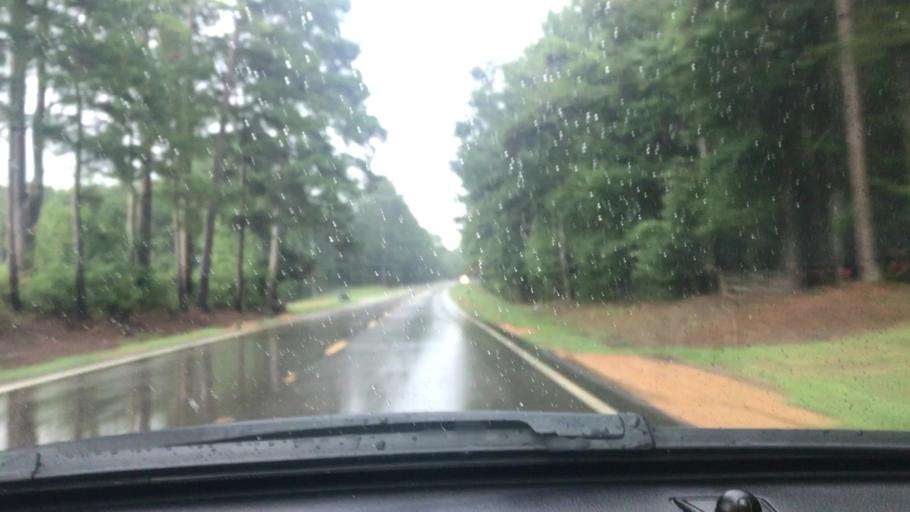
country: US
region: Mississippi
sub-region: Pike County
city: Summit
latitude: 31.3379
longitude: -90.5707
